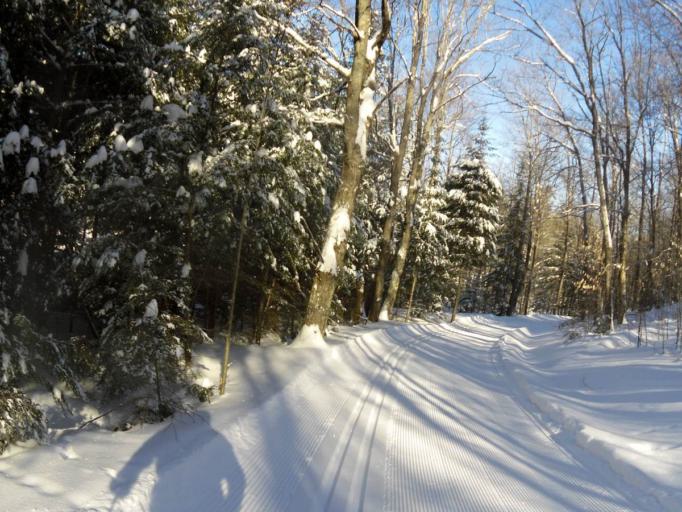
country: CA
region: Quebec
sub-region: Outaouais
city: Wakefield
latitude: 45.6013
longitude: -75.9640
